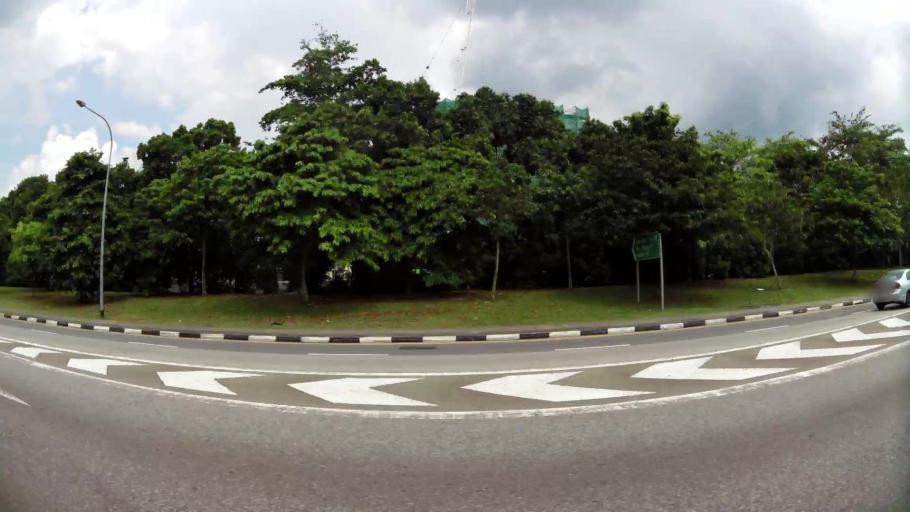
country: SG
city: Singapore
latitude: 1.2806
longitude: 103.7832
